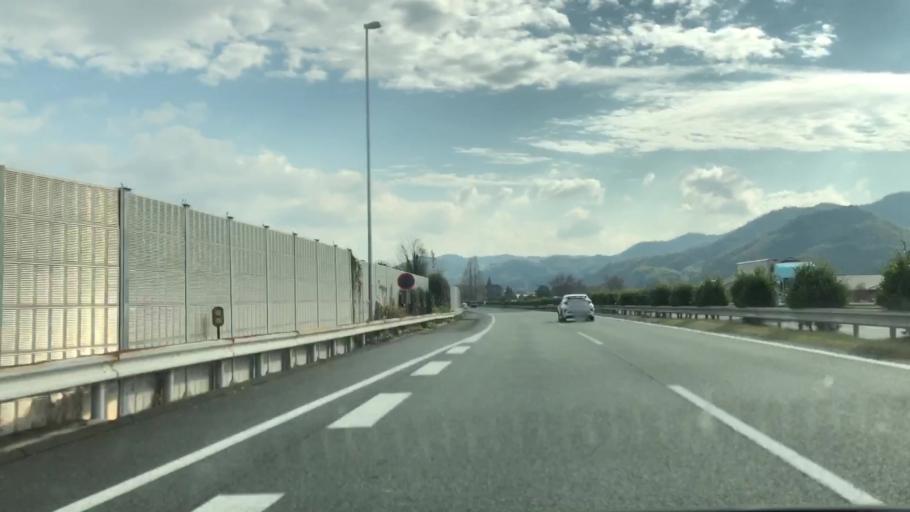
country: JP
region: Fukuoka
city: Setakamachi-takayanagi
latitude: 33.1253
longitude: 130.5185
